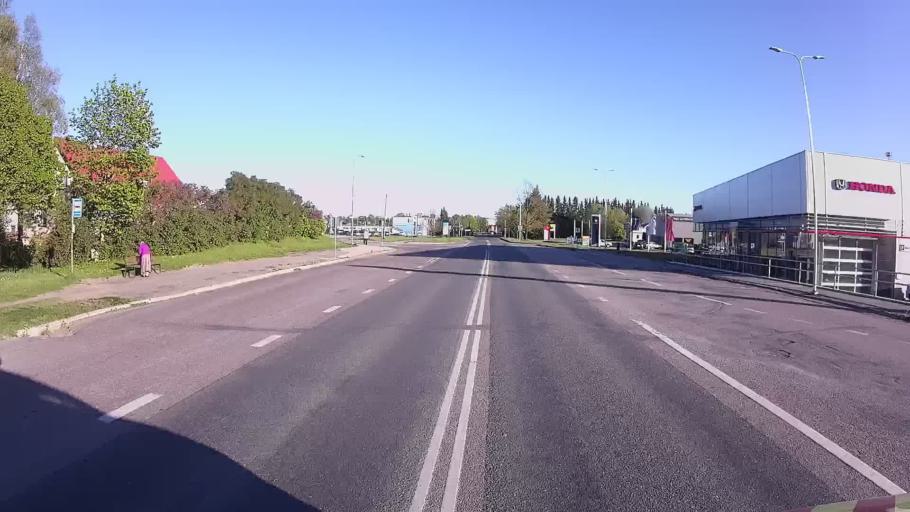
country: EE
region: Viljandimaa
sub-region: Viljandi linn
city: Viljandi
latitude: 58.3781
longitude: 25.5963
